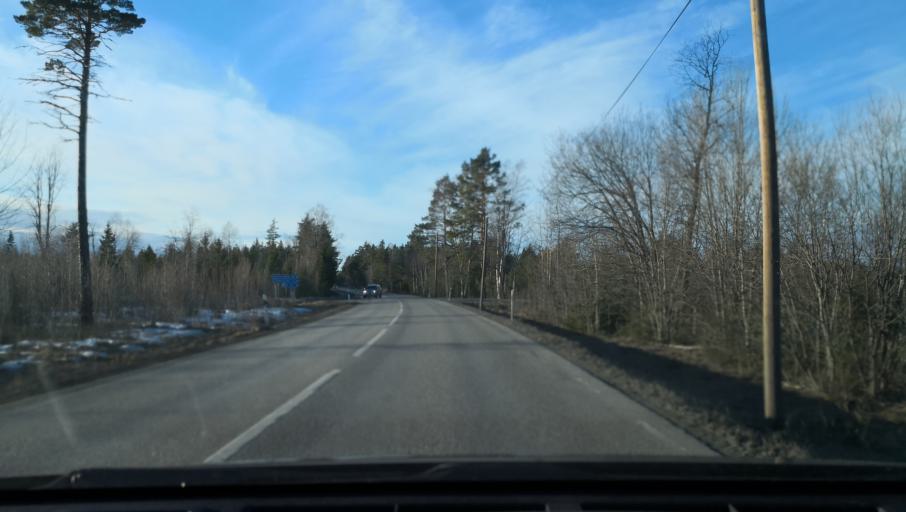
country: SE
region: Uppsala
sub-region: Osthammars Kommun
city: OEsthammar
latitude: 60.2659
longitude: 18.3335
